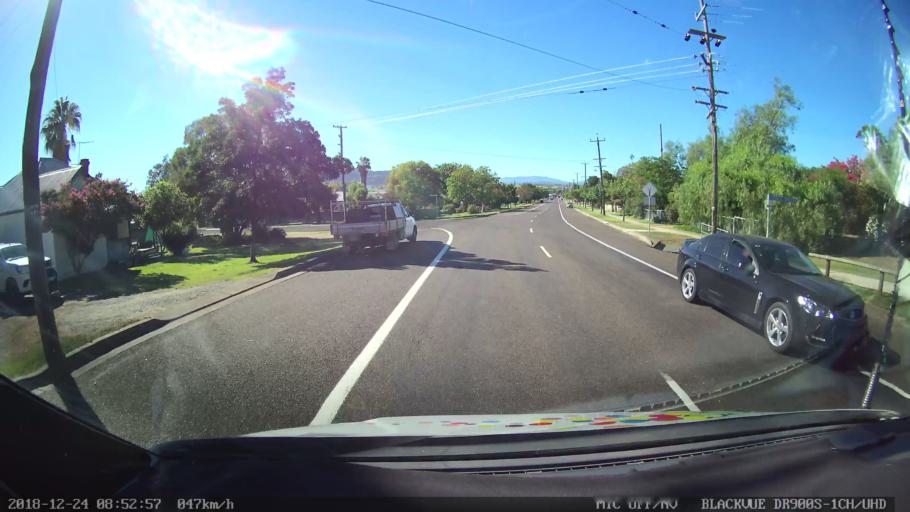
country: AU
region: New South Wales
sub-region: Liverpool Plains
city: Quirindi
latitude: -31.4948
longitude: 150.6807
